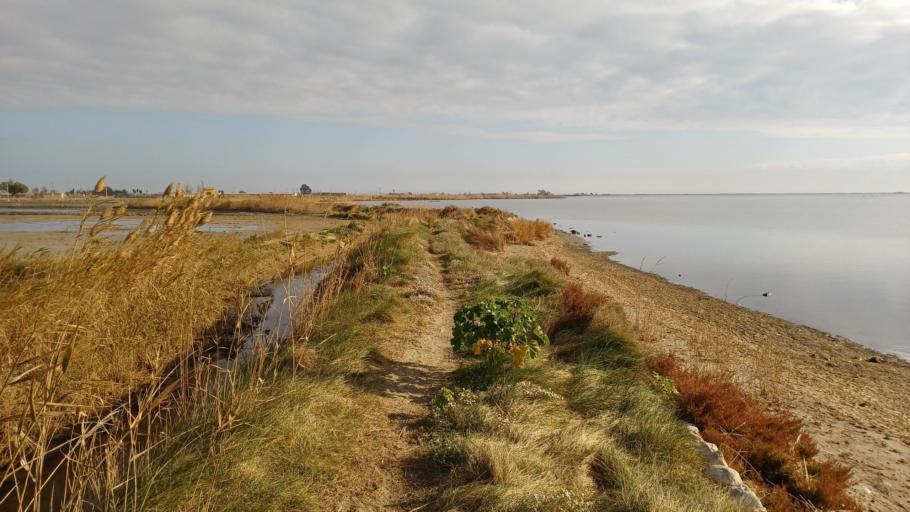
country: ES
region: Catalonia
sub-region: Provincia de Tarragona
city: Deltebre
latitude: 40.6365
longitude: 0.7083
